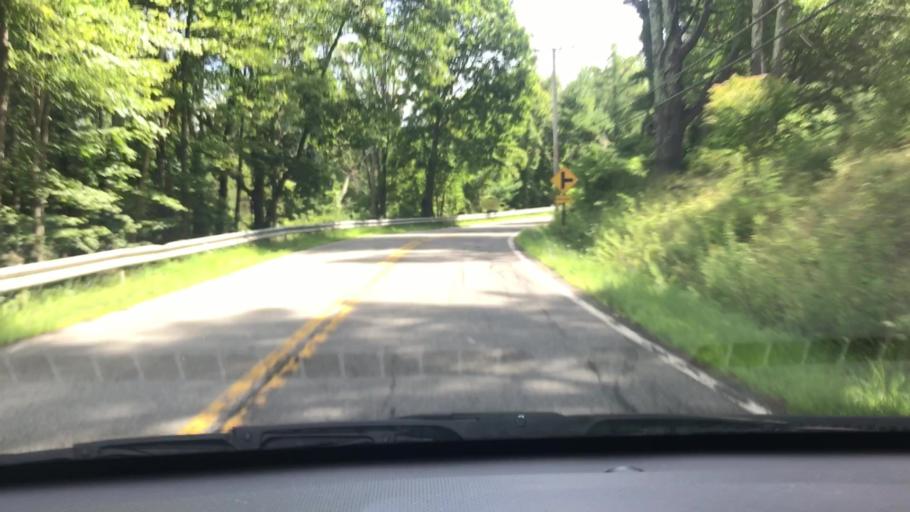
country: US
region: New York
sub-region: Ulster County
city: Shokan
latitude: 41.9174
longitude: -74.2059
